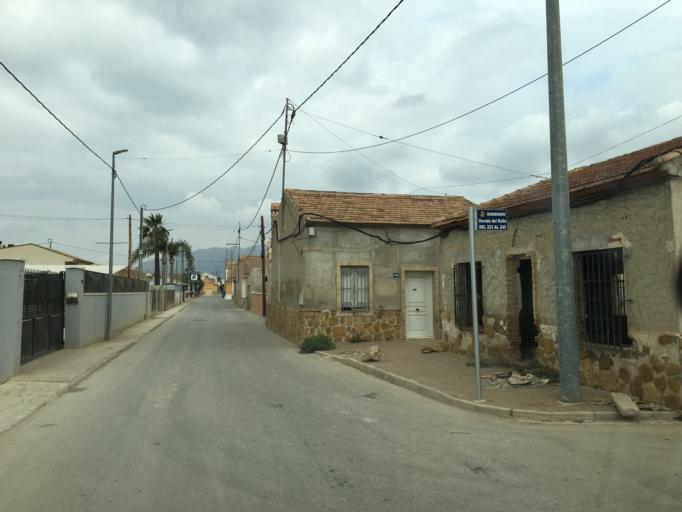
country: ES
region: Murcia
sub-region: Murcia
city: Beniel
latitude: 38.0370
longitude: -0.9869
